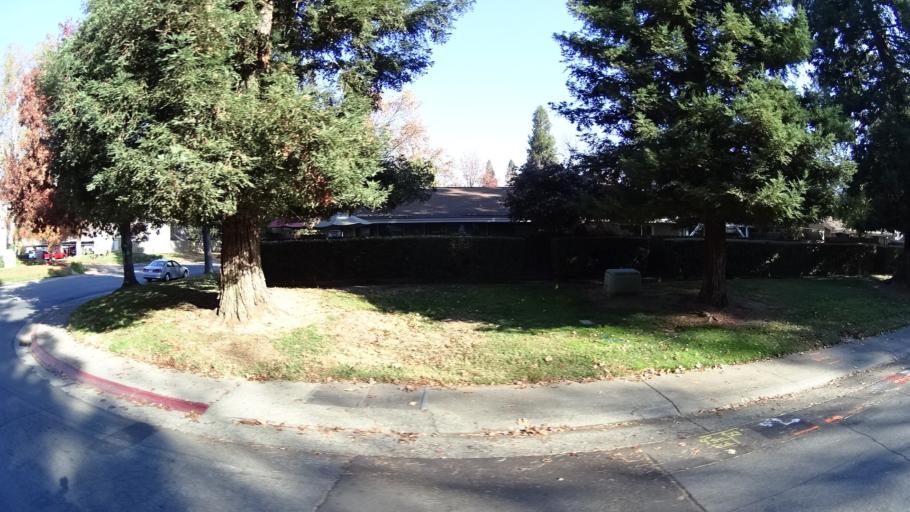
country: US
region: California
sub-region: Sacramento County
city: Citrus Heights
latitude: 38.6883
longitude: -121.3018
